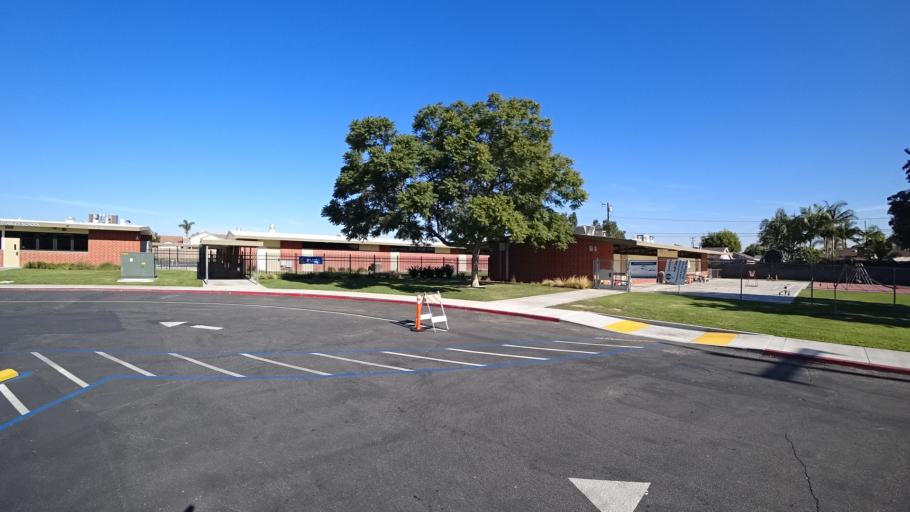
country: US
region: California
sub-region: Orange County
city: Garden Grove
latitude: 33.7853
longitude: -117.9374
